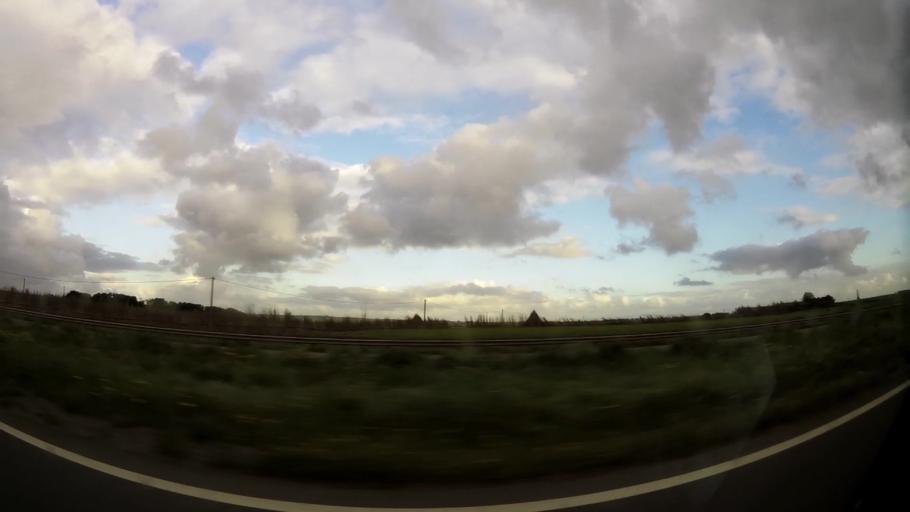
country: MA
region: Grand Casablanca
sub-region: Mediouna
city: Tit Mellil
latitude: 33.6016
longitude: -7.4380
